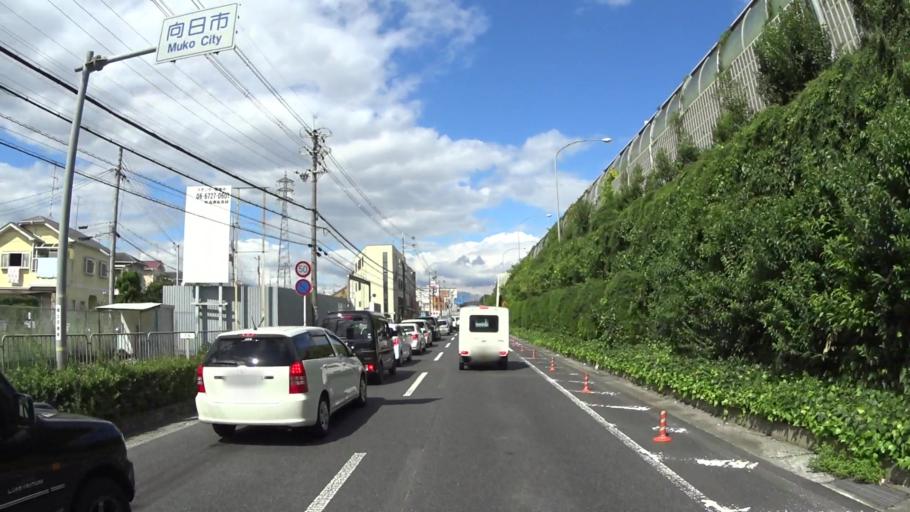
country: JP
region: Kyoto
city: Muko
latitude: 34.9290
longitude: 135.7125
